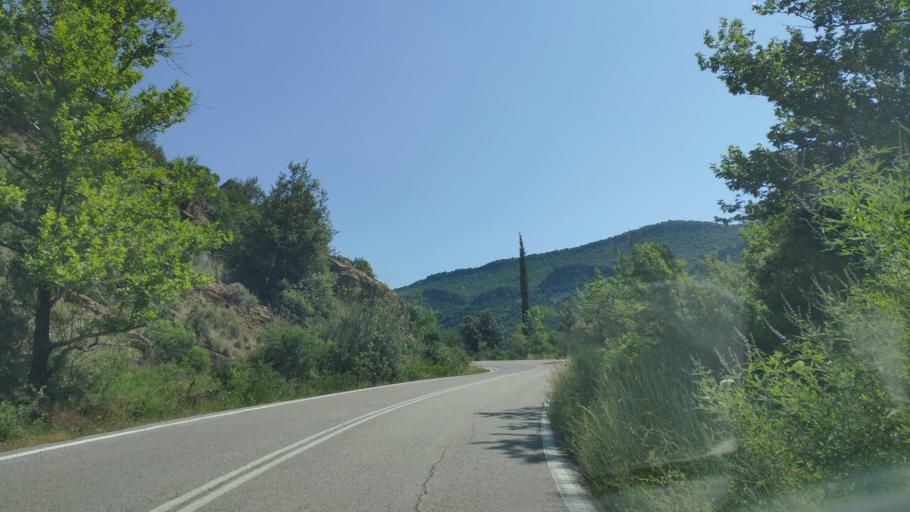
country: GR
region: West Greece
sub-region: Nomos Aitolias kai Akarnanias
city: Lepenou
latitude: 38.7724
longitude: 21.3352
